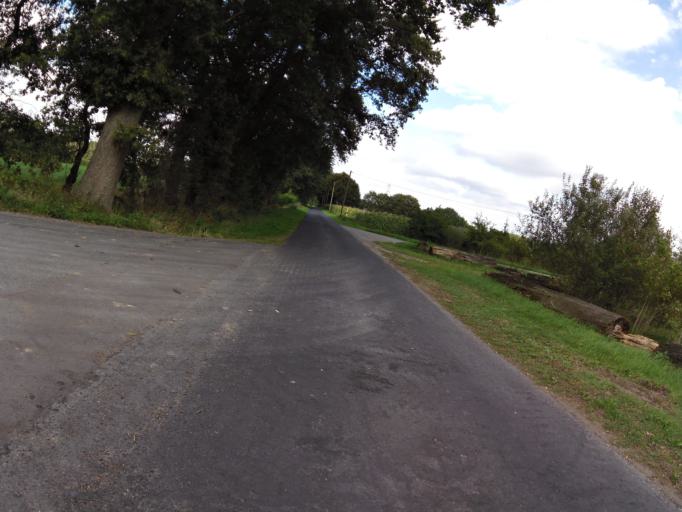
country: DE
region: North Rhine-Westphalia
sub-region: Regierungsbezirk Munster
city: Gronau
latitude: 52.1629
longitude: 7.0128
